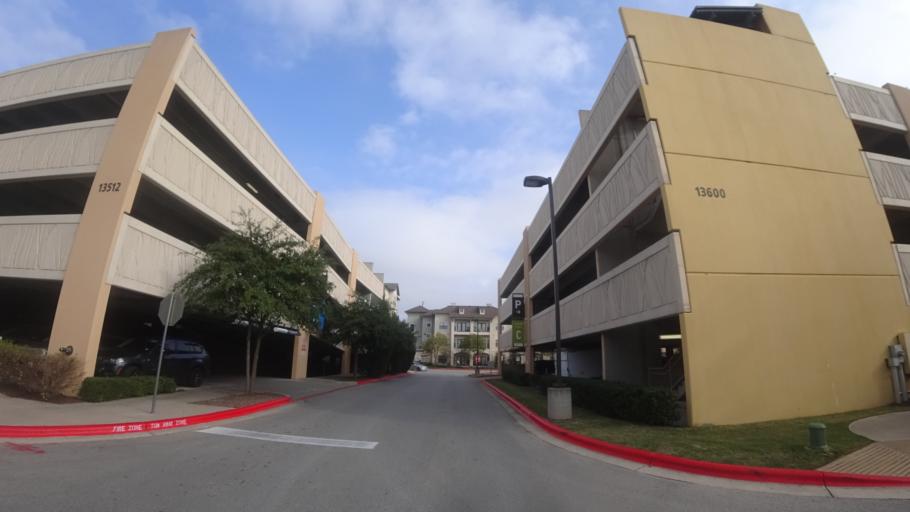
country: US
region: Texas
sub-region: Travis County
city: Bee Cave
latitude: 30.3086
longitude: -97.9379
